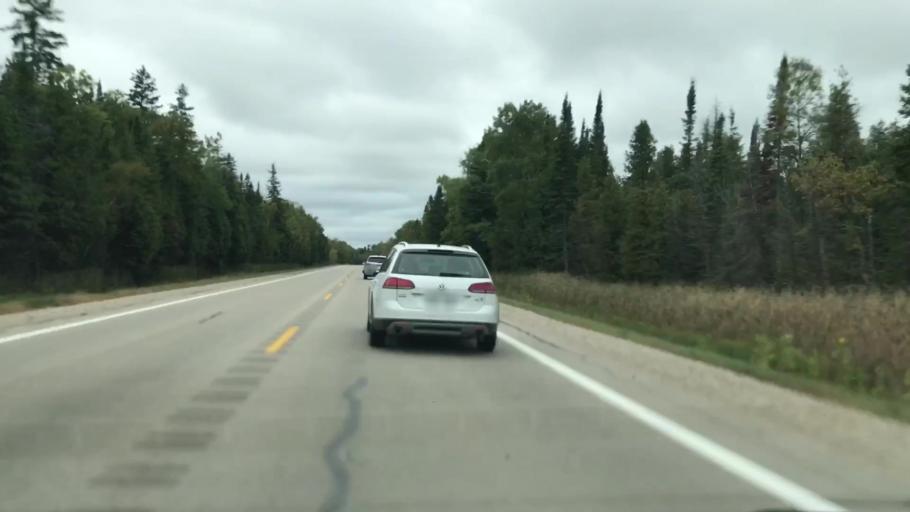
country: US
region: Michigan
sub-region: Delta County
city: Escanaba
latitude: 45.4408
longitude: -87.3431
